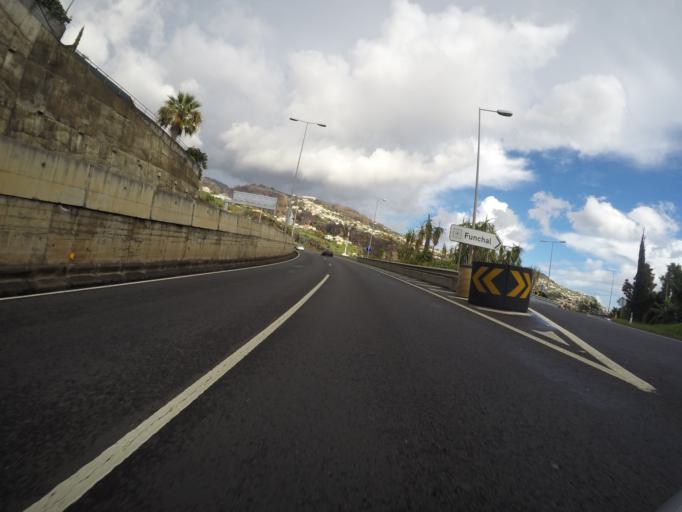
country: PT
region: Madeira
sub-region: Funchal
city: Nossa Senhora do Monte
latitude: 32.6615
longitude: -16.9052
